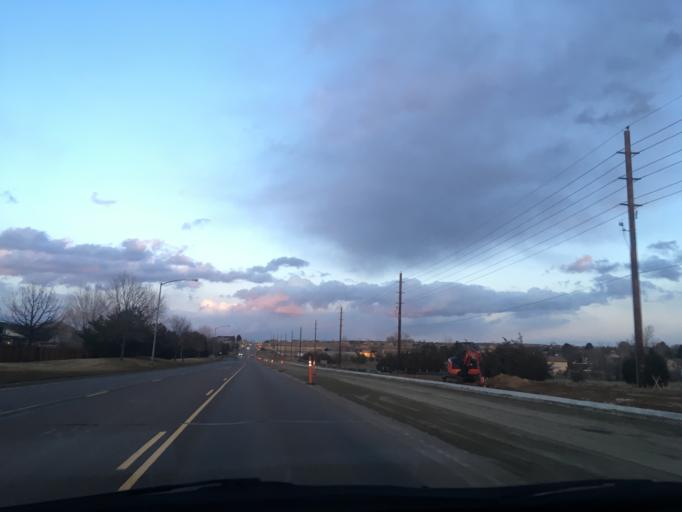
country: US
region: Colorado
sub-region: Adams County
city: Northglenn
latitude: 39.9575
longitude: -104.9665
